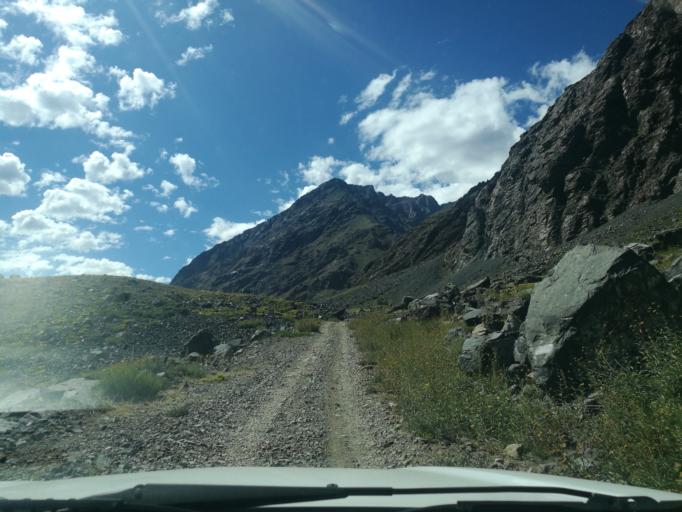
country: CL
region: O'Higgins
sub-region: Provincia de Cachapoal
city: Machali
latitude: -34.4082
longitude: -70.2425
